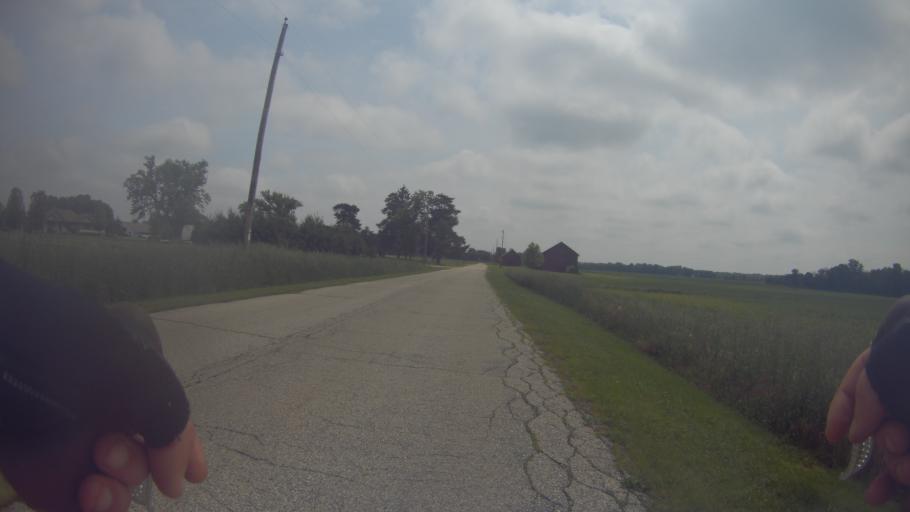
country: US
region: Wisconsin
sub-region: Jefferson County
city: Lake Ripley
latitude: 42.9324
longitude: -88.9932
